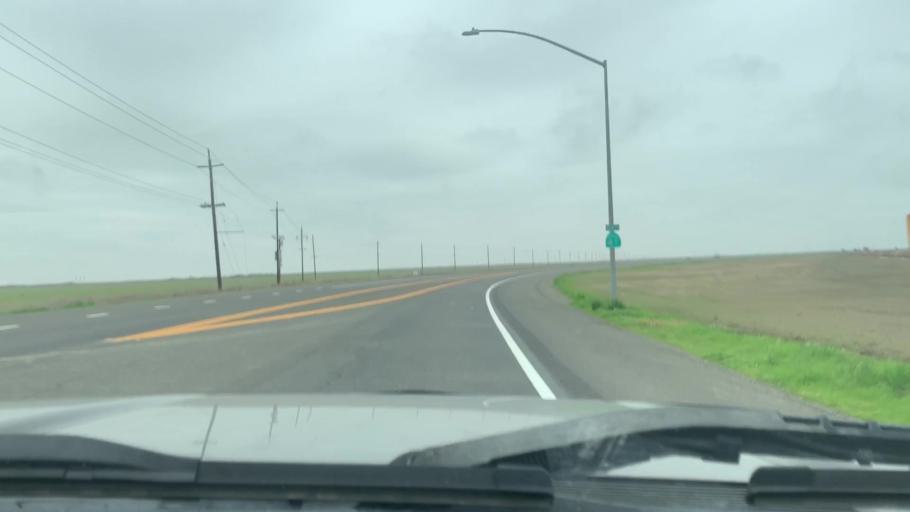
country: US
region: California
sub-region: Kings County
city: Kettleman City
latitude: 36.0364
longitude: -119.9589
